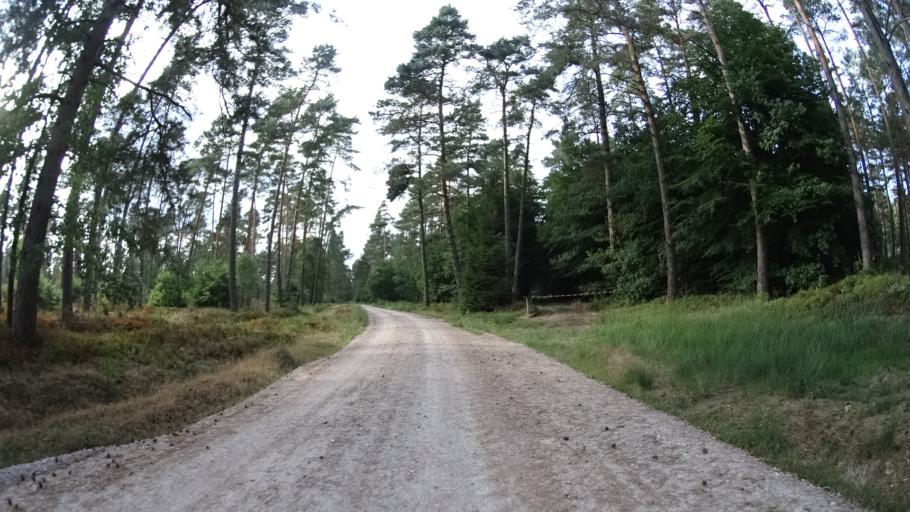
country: DE
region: Lower Saxony
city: Handeloh
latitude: 53.1926
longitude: 9.8834
